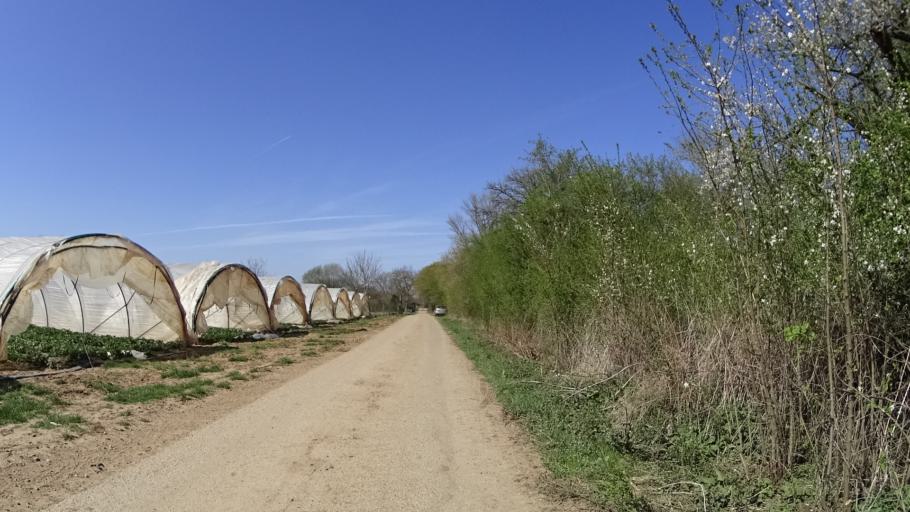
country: DE
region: Baden-Wuerttemberg
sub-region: Karlsruhe Region
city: Dossenheim
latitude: 49.4389
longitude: 8.6584
